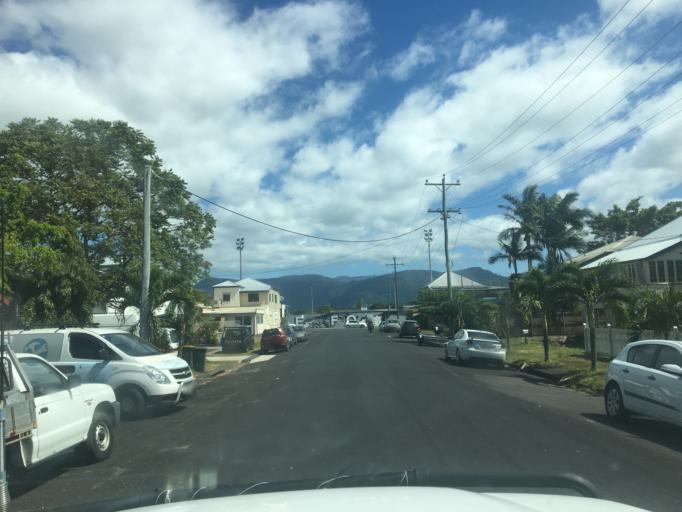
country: AU
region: Queensland
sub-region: Cairns
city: Cairns
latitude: -16.9256
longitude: 145.7662
